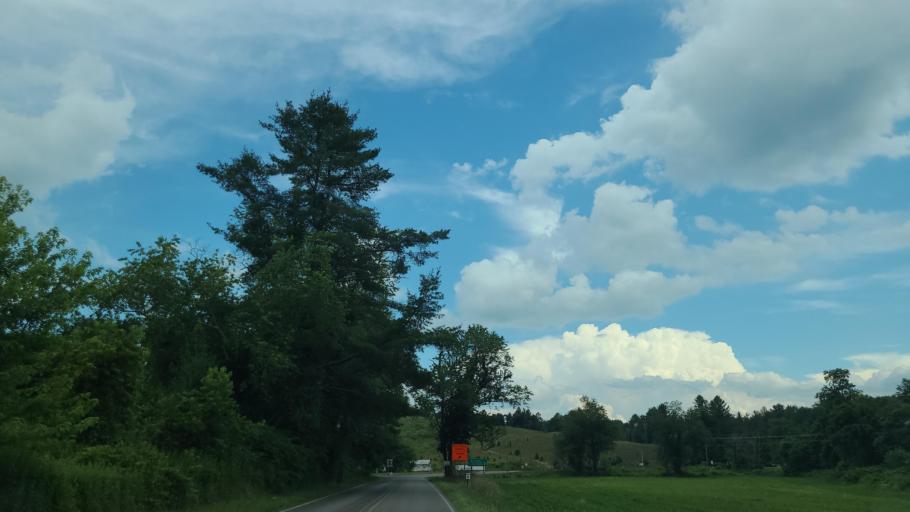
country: US
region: North Carolina
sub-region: Alleghany County
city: Sparta
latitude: 36.4138
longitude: -81.2649
